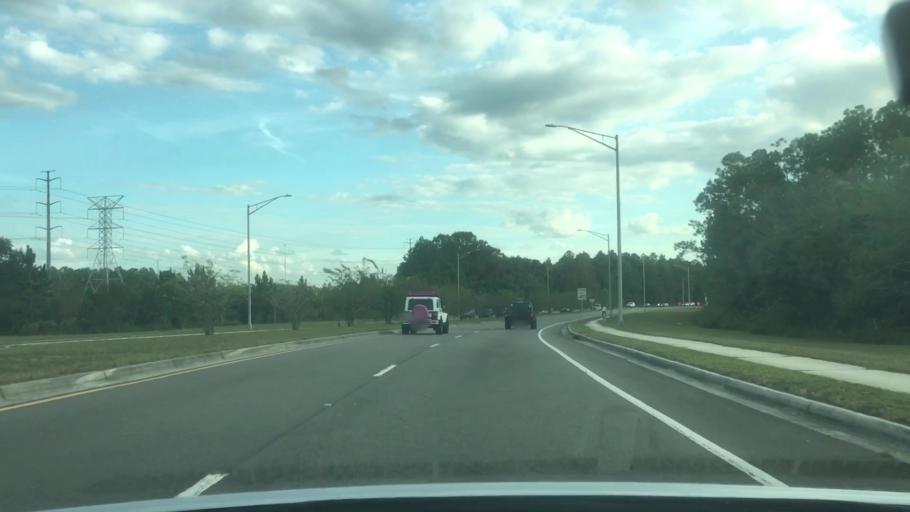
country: US
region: Florida
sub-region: Duval County
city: Jacksonville Beach
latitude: 30.2770
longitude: -81.5237
